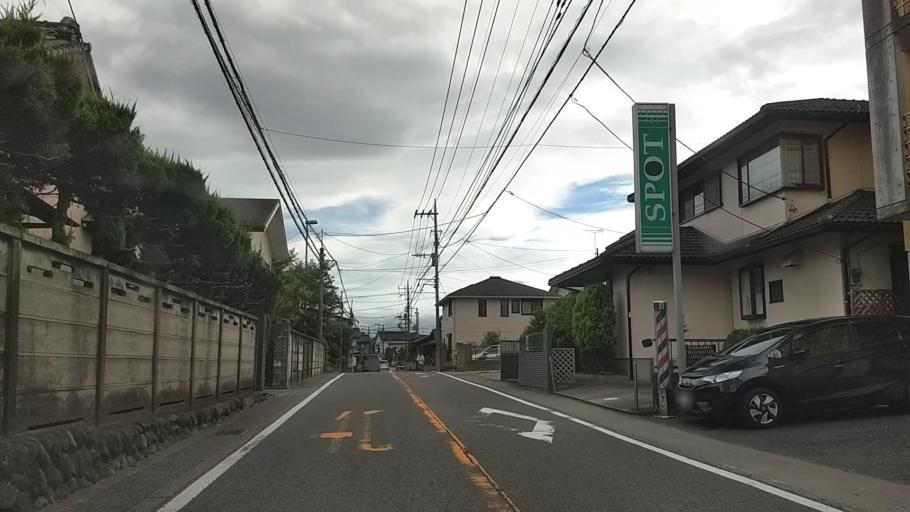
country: JP
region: Tokyo
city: Hachioji
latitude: 35.6050
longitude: 139.3155
